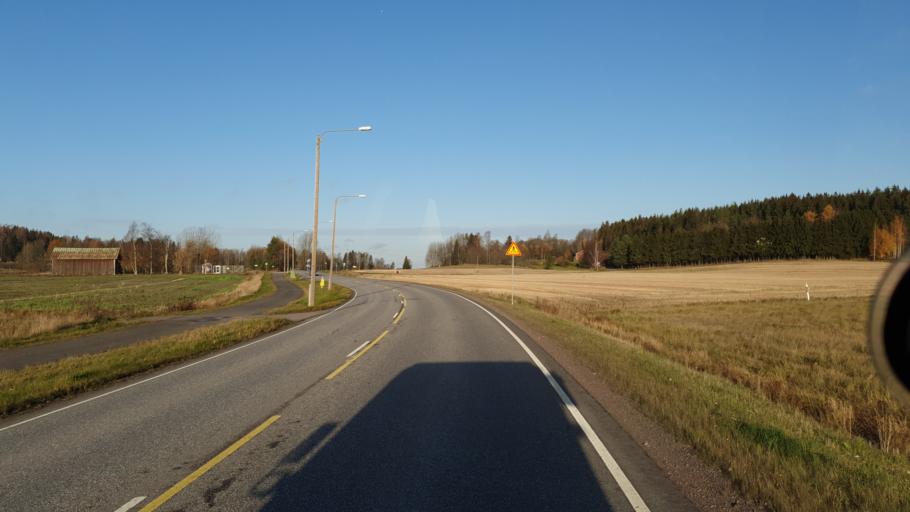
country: FI
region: Uusimaa
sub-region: Helsinki
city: Siuntio
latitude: 60.1490
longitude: 24.2144
